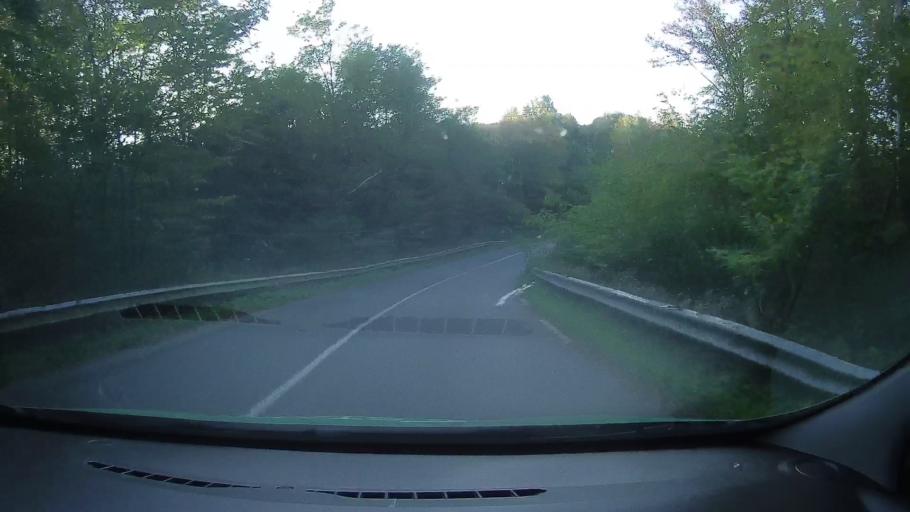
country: RO
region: Timis
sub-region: Comuna Fardea
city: Fardea
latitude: 45.7473
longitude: 22.1356
